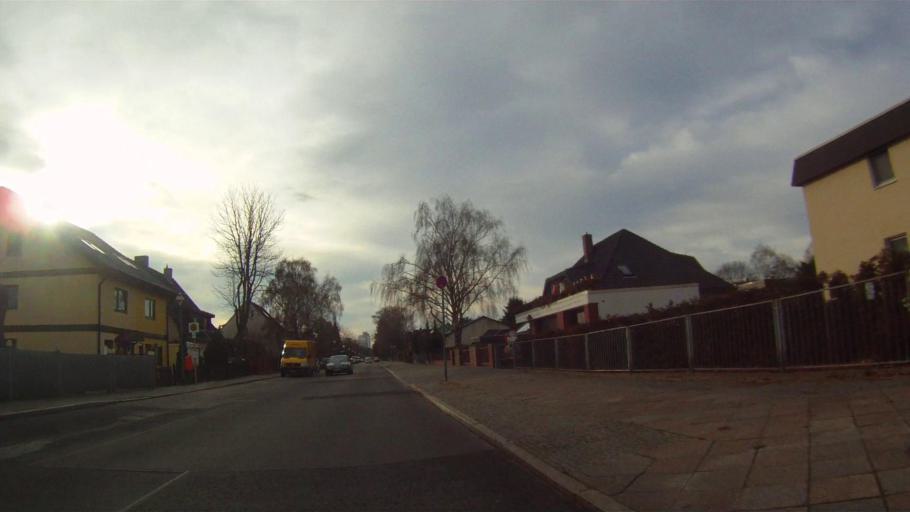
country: DE
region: Berlin
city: Rudow
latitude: 52.4350
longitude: 13.4879
